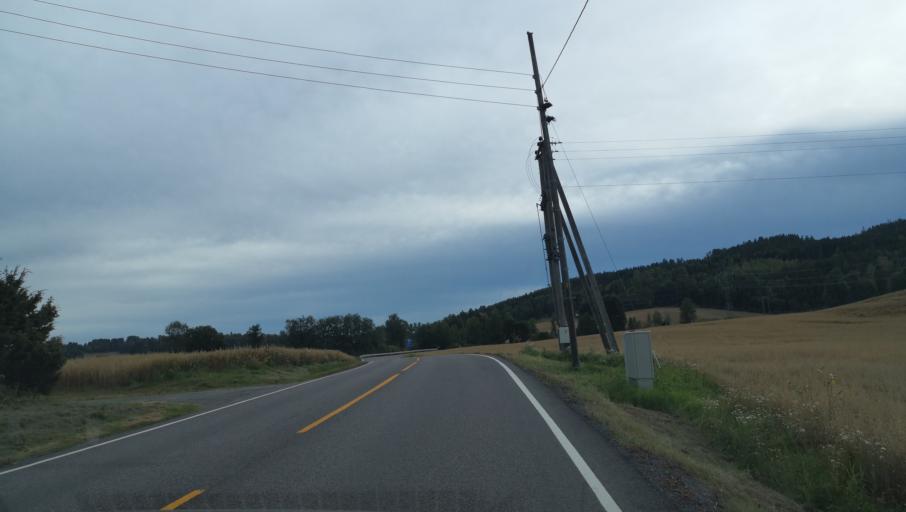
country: NO
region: Ostfold
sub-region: Hobol
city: Tomter
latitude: 59.6957
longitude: 11.0412
